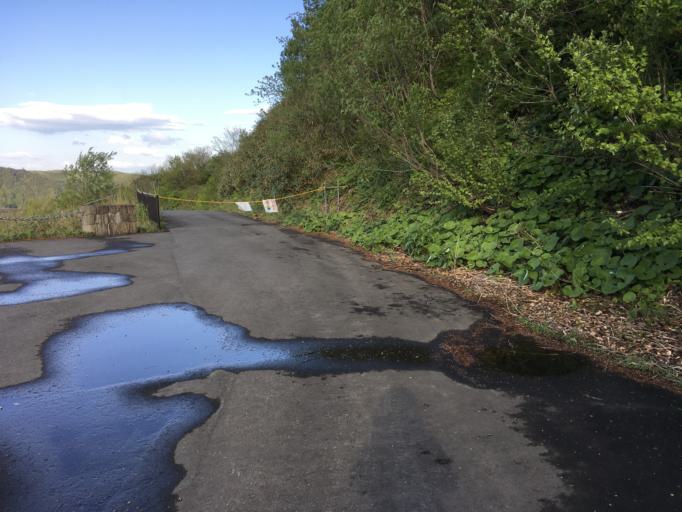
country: JP
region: Iwate
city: Mizusawa
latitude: 39.1180
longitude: 140.9208
